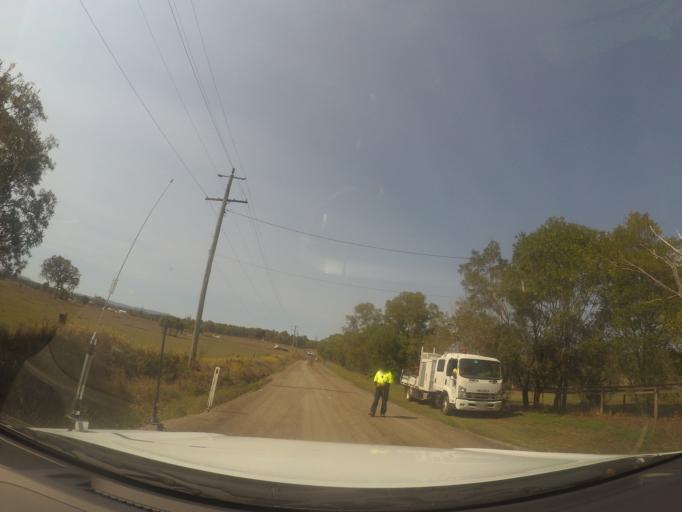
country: AU
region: Queensland
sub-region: Logan
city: Chambers Flat
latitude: -27.7633
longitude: 153.0589
